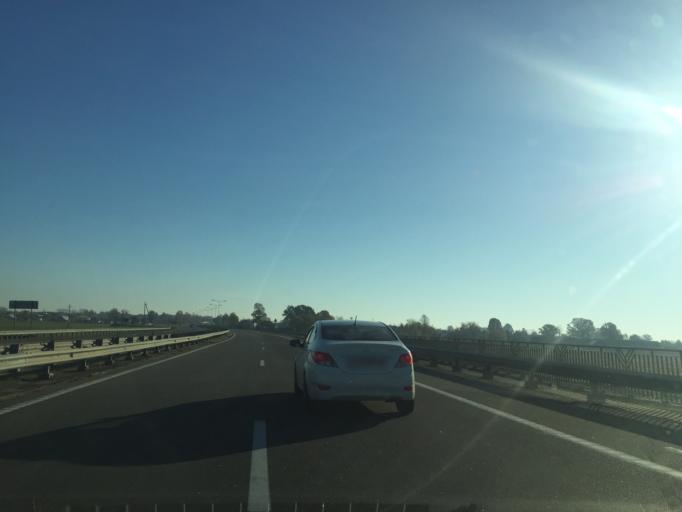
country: BY
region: Minsk
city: Smilavichy
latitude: 53.7582
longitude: 27.9683
